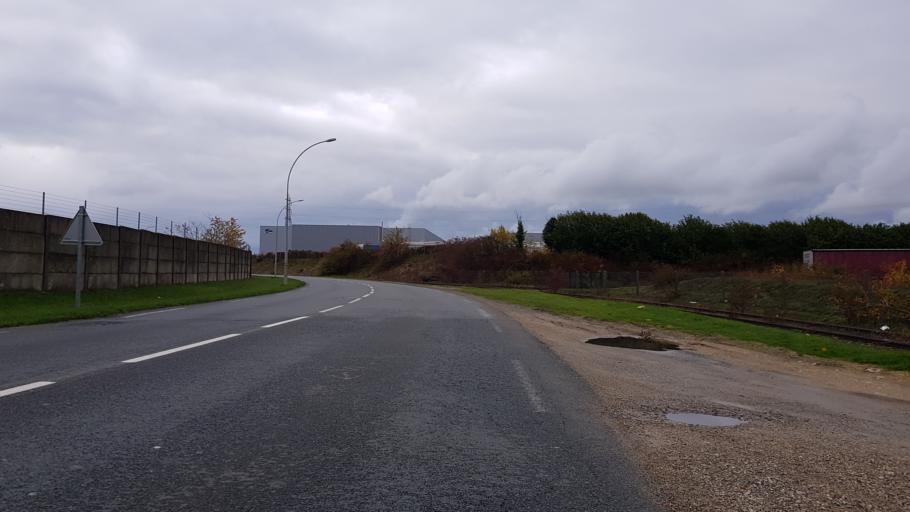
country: FR
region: Poitou-Charentes
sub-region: Departement de la Vienne
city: Chasseneuil-du-Poitou
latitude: 46.6662
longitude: 0.3759
